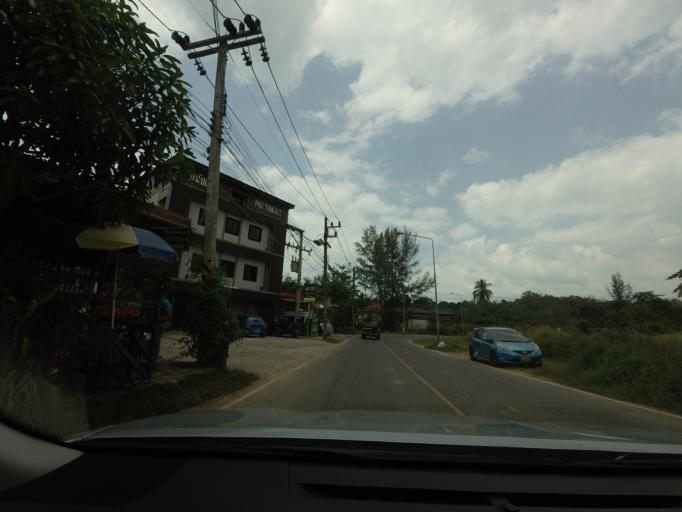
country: TH
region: Phangnga
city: Ban Ao Nang
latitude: 8.0796
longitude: 98.7439
